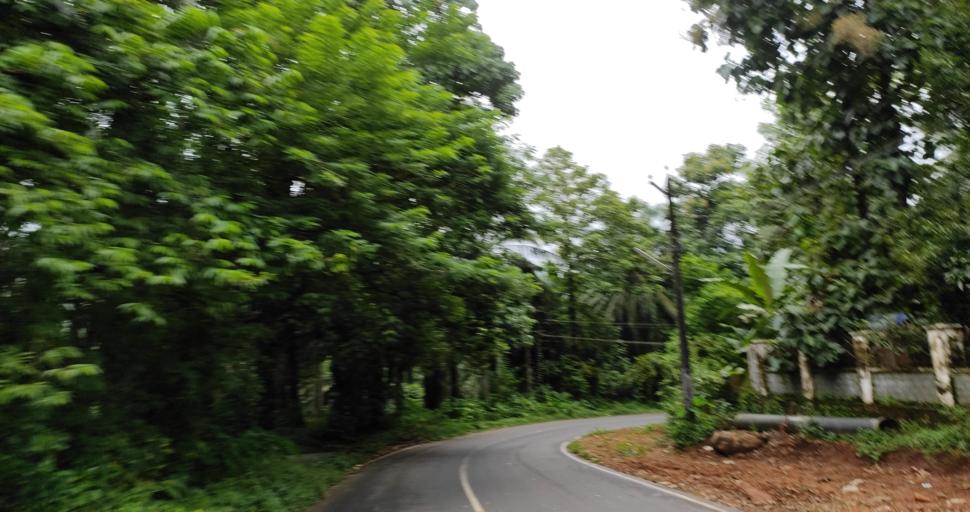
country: IN
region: Kerala
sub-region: Ernakulam
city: Angamali
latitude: 10.2908
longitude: 76.5045
